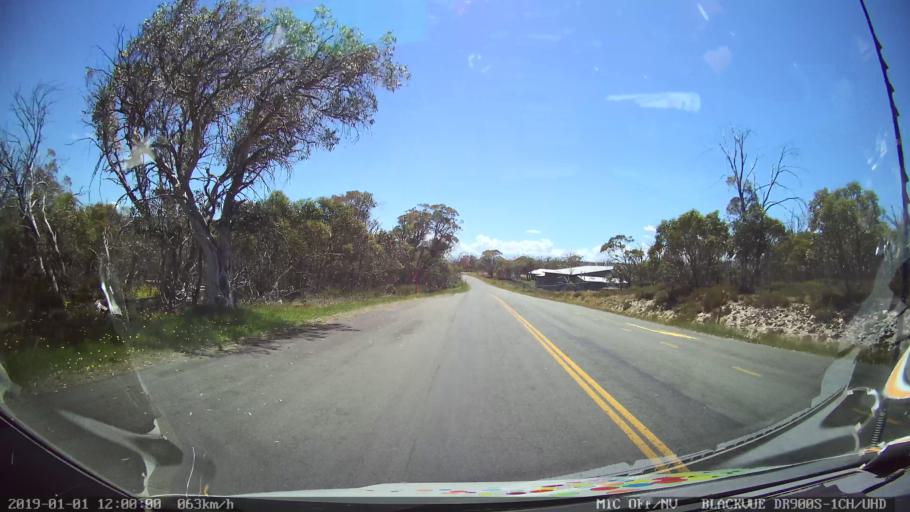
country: AU
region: New South Wales
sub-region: Snowy River
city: Jindabyne
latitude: -35.8881
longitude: 148.4564
